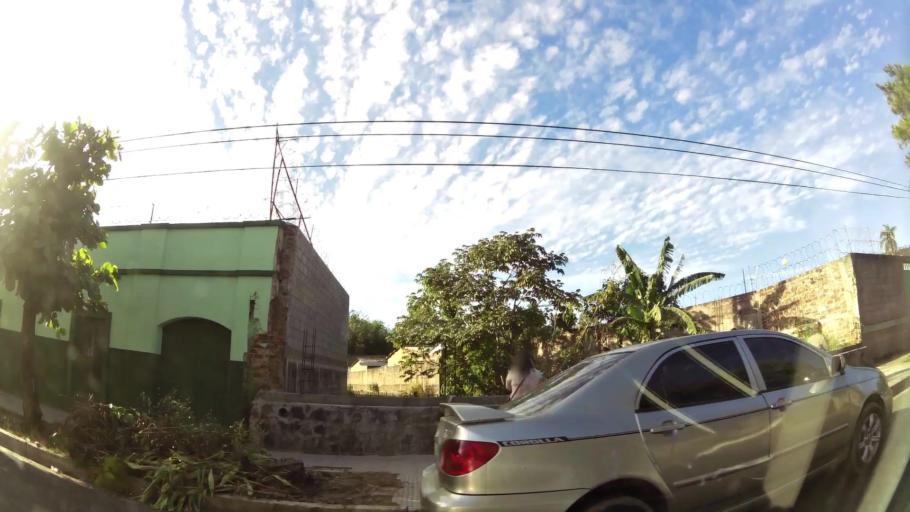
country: SV
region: Santa Ana
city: Santa Ana
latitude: 13.9985
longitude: -89.5625
